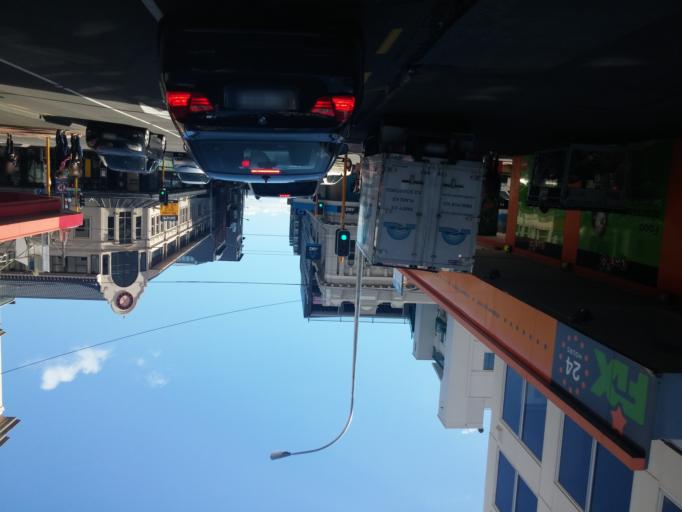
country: NZ
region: Wellington
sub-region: Wellington City
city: Wellington
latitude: -41.2937
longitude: 174.7810
